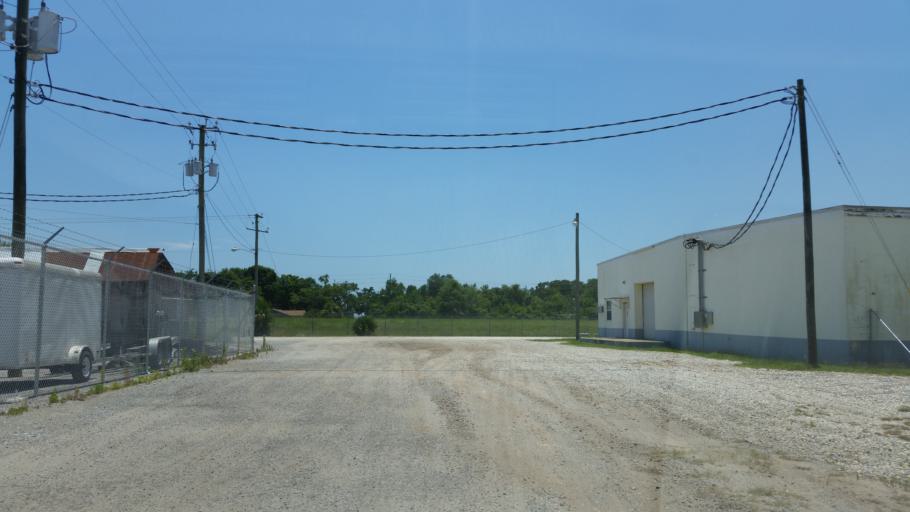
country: US
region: Florida
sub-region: Escambia County
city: Pensacola
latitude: 30.4052
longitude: -87.2355
